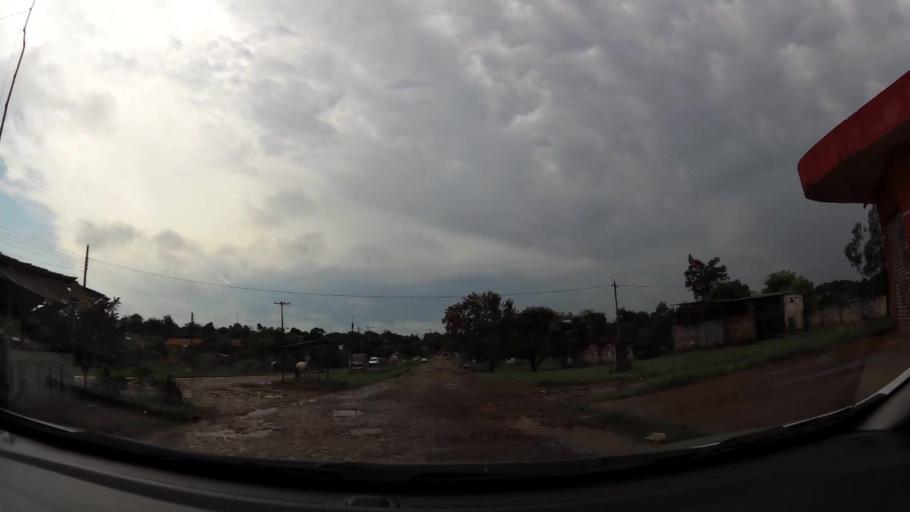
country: PY
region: Alto Parana
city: Presidente Franco
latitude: -25.5325
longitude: -54.6691
